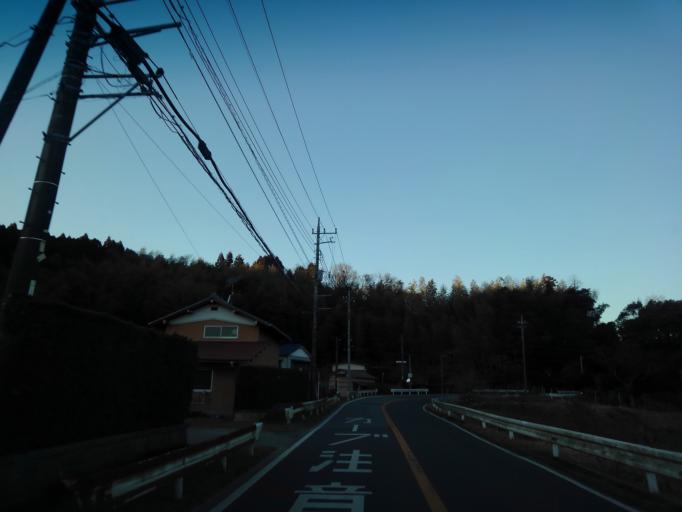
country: JP
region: Chiba
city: Kimitsu
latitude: 35.2918
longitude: 139.9772
